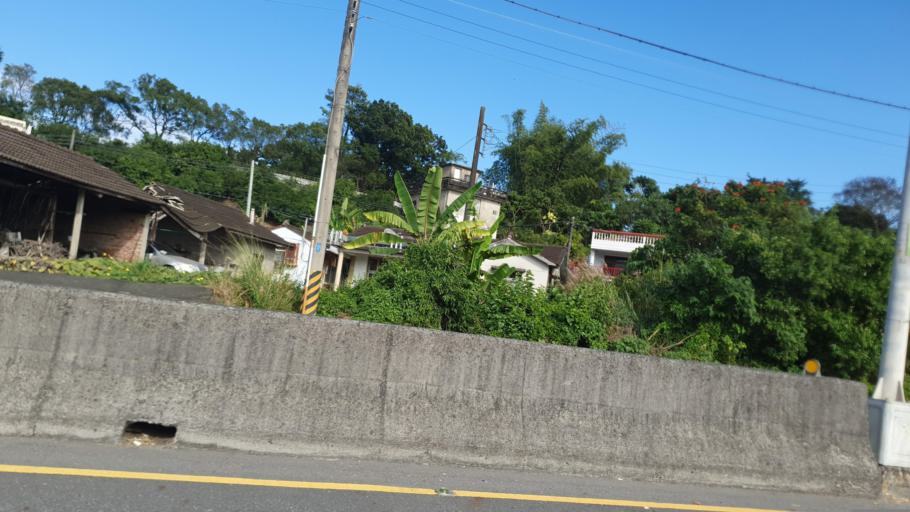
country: TW
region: Taiwan
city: Yujing
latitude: 23.0544
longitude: 120.4029
